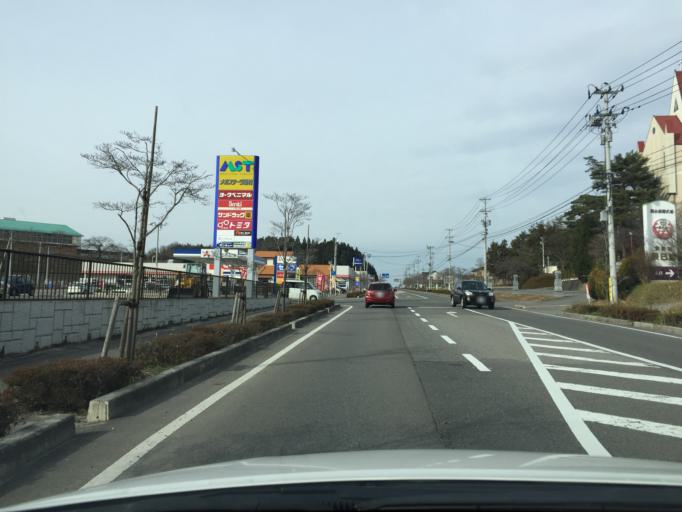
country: JP
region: Fukushima
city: Funehikimachi-funehiki
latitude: 37.4478
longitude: 140.5830
